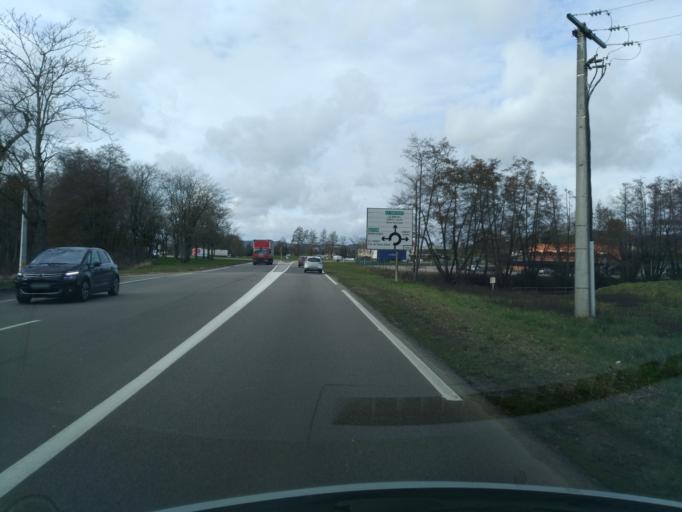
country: FR
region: Bourgogne
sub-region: Departement de Saone-et-Loire
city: Torcy
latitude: 46.7666
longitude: 4.4544
